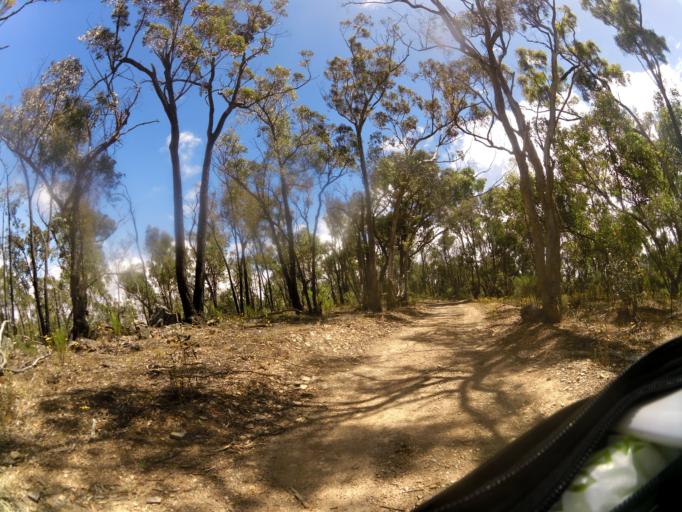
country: AU
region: Victoria
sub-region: Mount Alexander
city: Castlemaine
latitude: -37.0683
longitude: 144.2651
